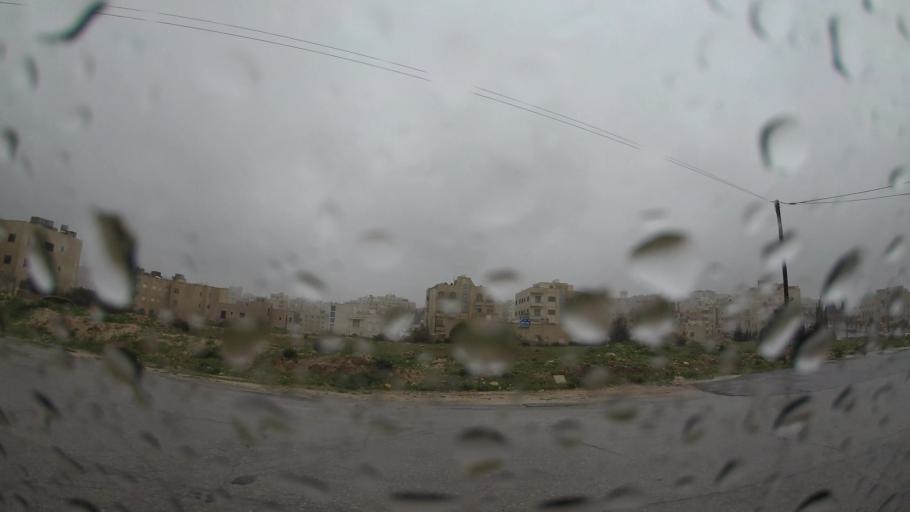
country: JO
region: Amman
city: Al Jubayhah
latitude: 32.0137
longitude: 35.8951
